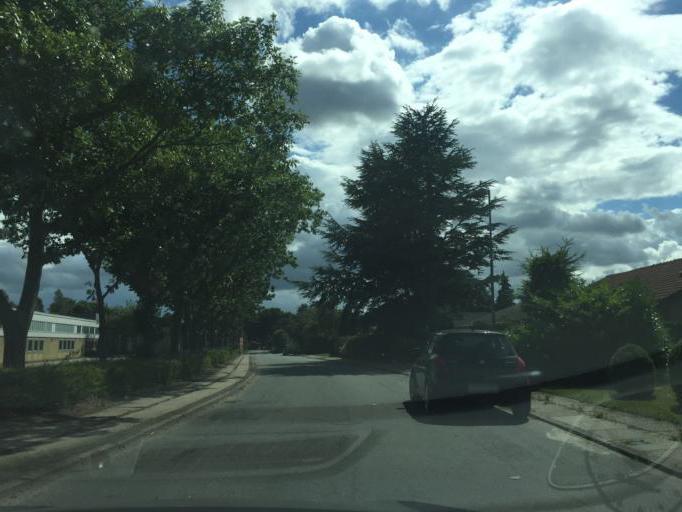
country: DK
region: South Denmark
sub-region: Nordfyns Kommune
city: Otterup
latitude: 55.5122
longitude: 10.3942
